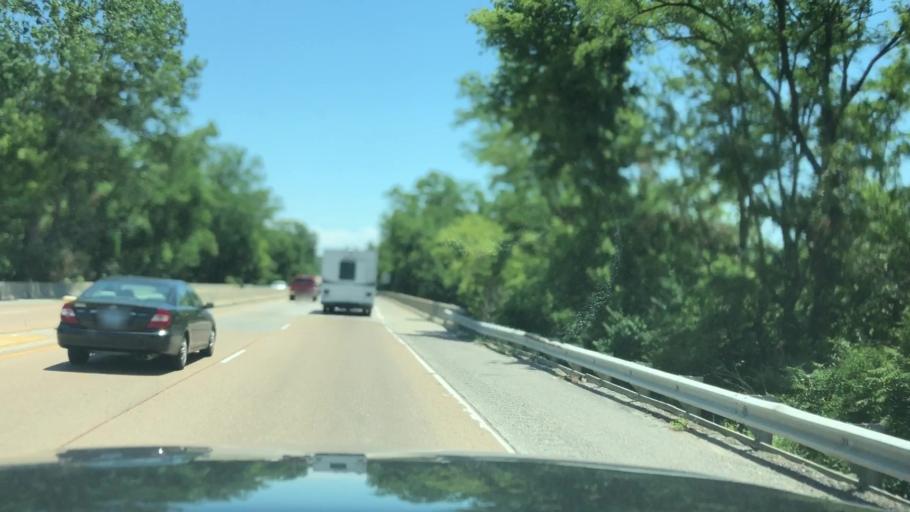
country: US
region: Illinois
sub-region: Saint Clair County
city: Alorton
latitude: 38.5599
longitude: -90.0831
